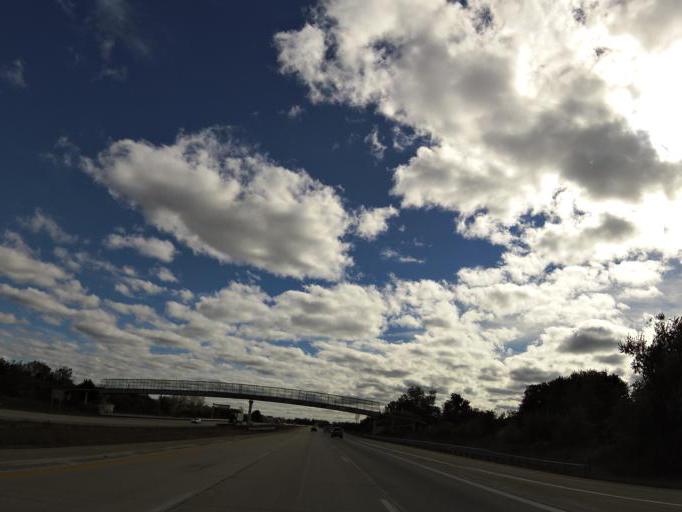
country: US
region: Michigan
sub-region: Genesee County
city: Burton
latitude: 43.0195
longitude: -83.5910
